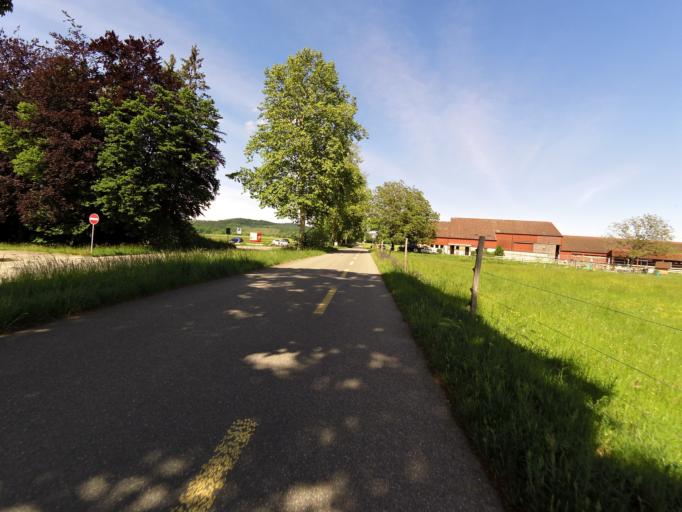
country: CH
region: Thurgau
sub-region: Frauenfeld District
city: Frauenfeld
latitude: 47.5733
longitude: 8.9070
